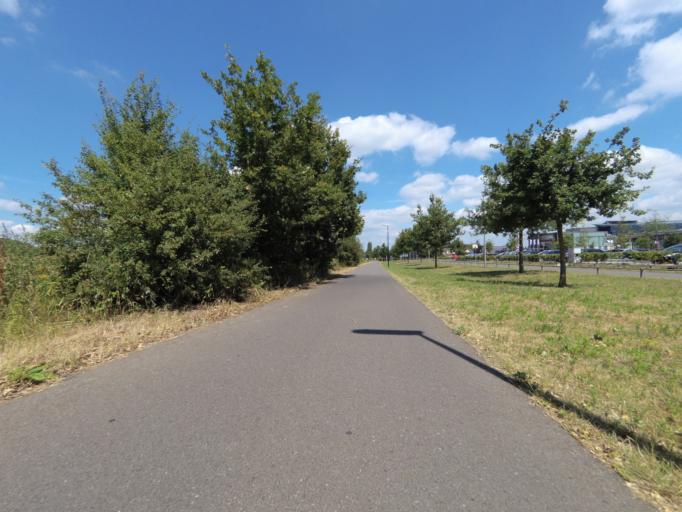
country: NL
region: Overijssel
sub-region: Gemeente Deventer
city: Schalkhaar
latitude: 52.2606
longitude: 6.1884
